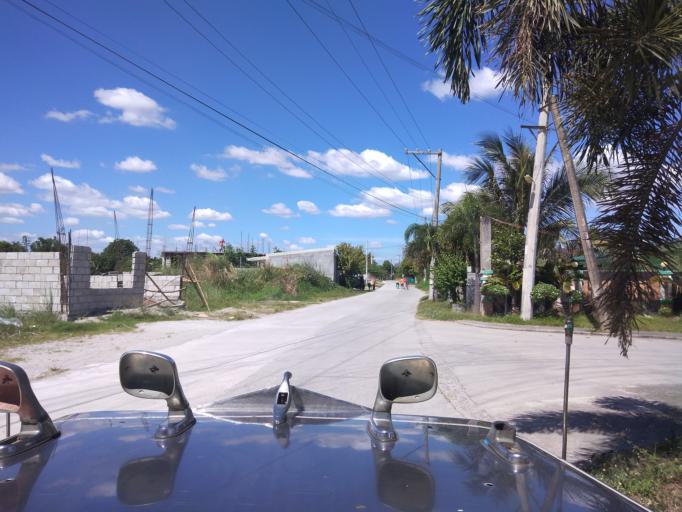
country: PH
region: Central Luzon
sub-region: Province of Pampanga
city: Magliman
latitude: 15.0282
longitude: 120.6507
